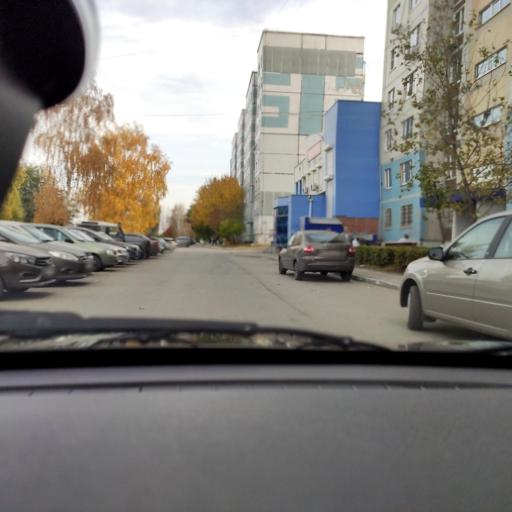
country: RU
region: Samara
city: Tol'yatti
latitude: 53.5471
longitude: 49.3513
